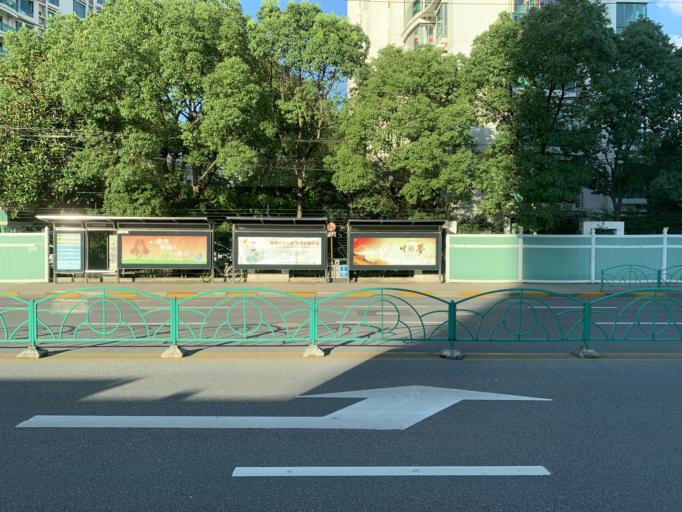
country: CN
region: Shanghai Shi
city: Huamu
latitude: 31.2228
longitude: 121.5473
